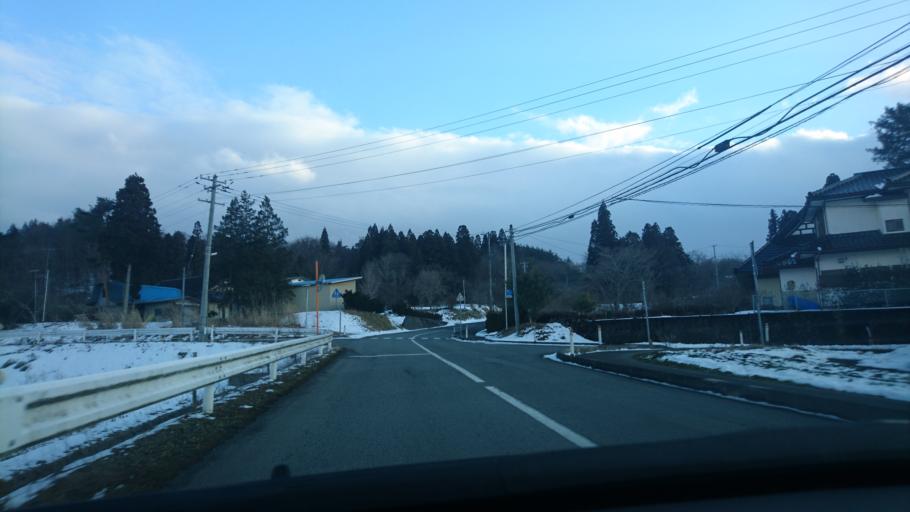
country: JP
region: Iwate
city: Ichinoseki
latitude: 39.0160
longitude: 141.3391
